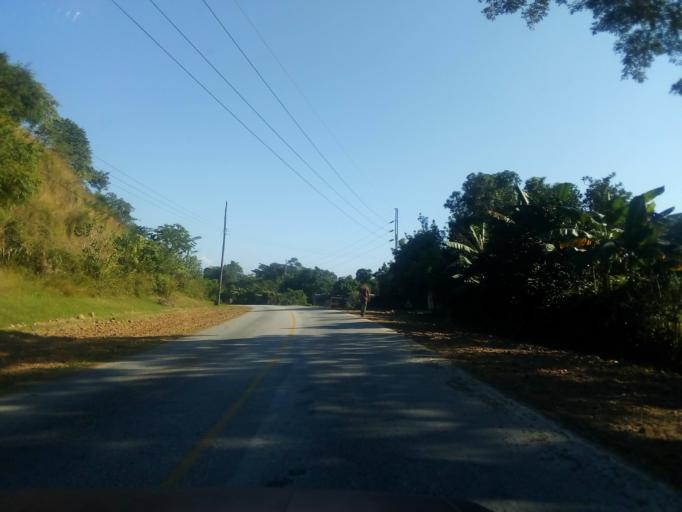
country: CU
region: Santiago de Cuba
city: Segundo Frente
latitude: 20.3669
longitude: -75.5540
